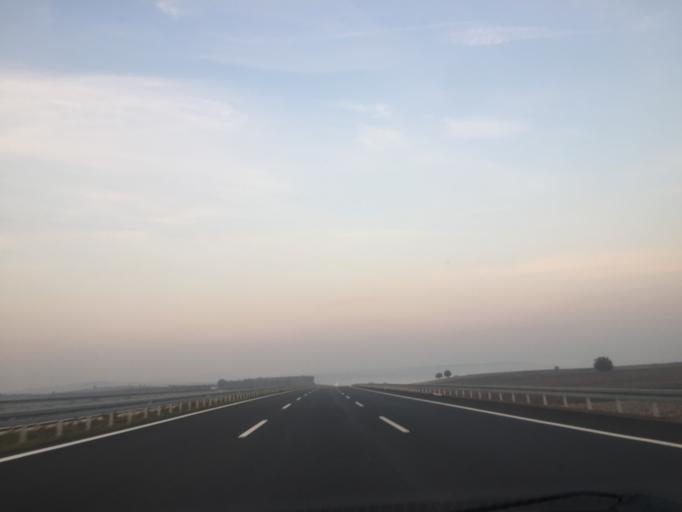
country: TR
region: Bursa
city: Mahmudiye
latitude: 40.2580
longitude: 28.6909
